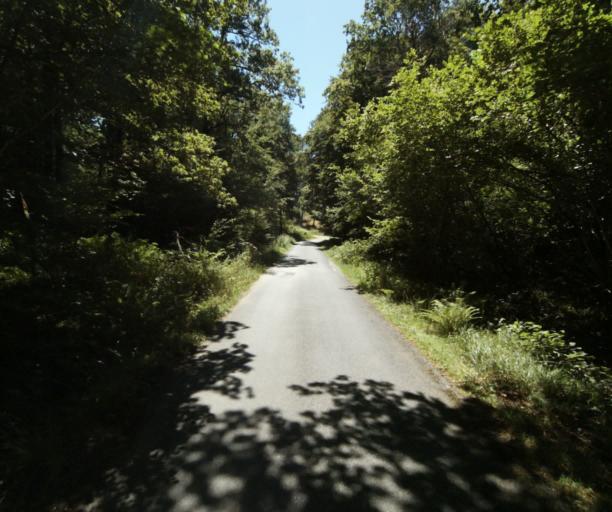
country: FR
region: Midi-Pyrenees
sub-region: Departement du Tarn
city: Dourgne
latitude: 43.4171
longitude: 2.1875
